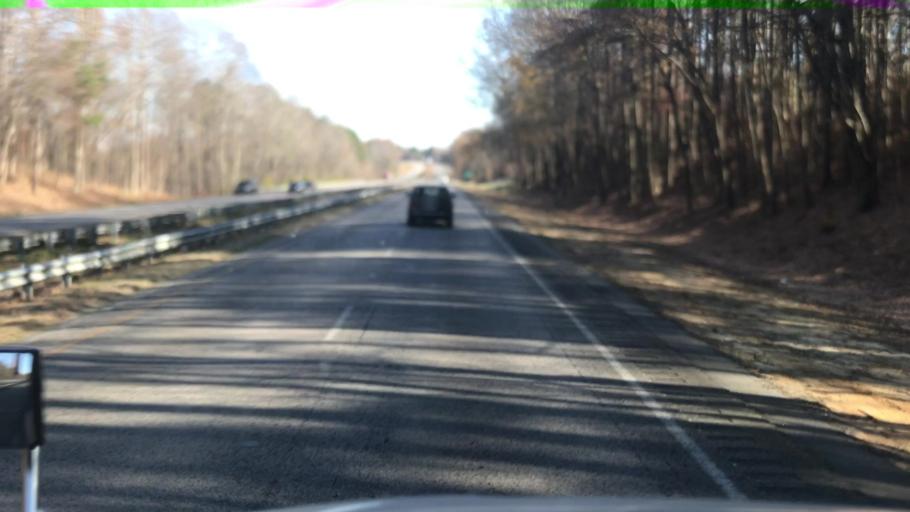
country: US
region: North Carolina
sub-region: Nash County
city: Nashville
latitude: 35.9768
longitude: -77.9243
